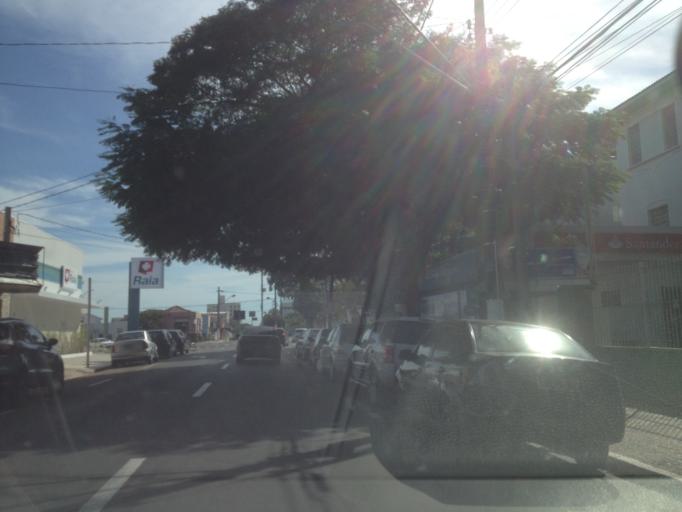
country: BR
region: Sao Paulo
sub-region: Marilia
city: Marilia
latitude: -22.2125
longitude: -49.9393
